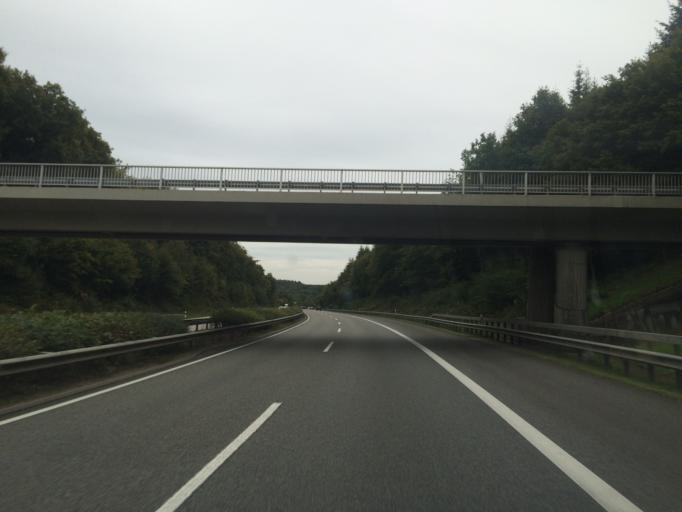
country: DE
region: Rheinland-Pfalz
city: Willwerscheid
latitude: 50.0278
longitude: 6.9207
